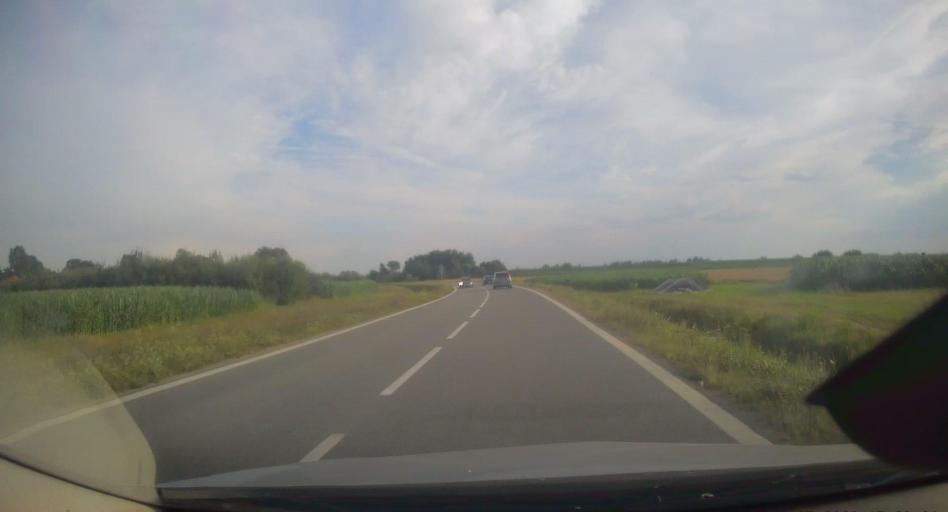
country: PL
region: Lesser Poland Voivodeship
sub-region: Powiat brzeski
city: Szczurowa
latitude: 50.1417
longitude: 20.6124
